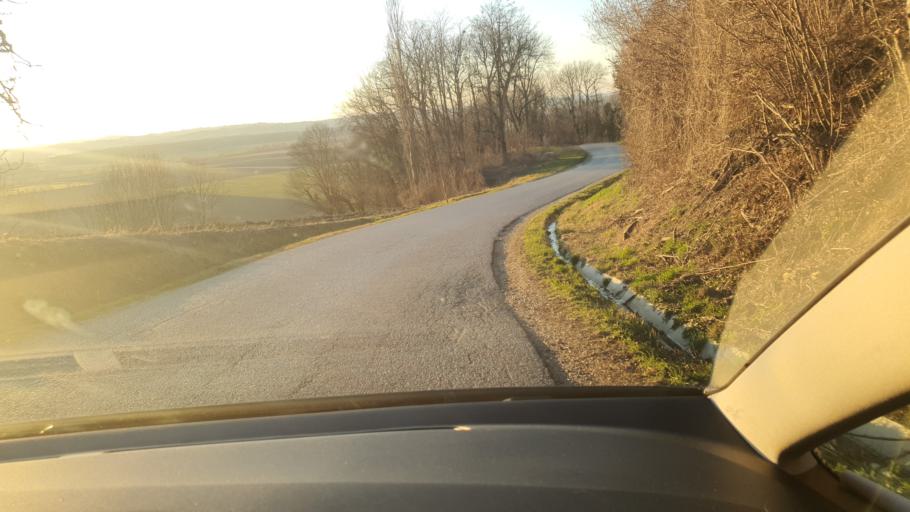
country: SI
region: Sveti Andraz v Slovenskih Goricah
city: Vitomarci
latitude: 46.5309
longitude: 15.9307
